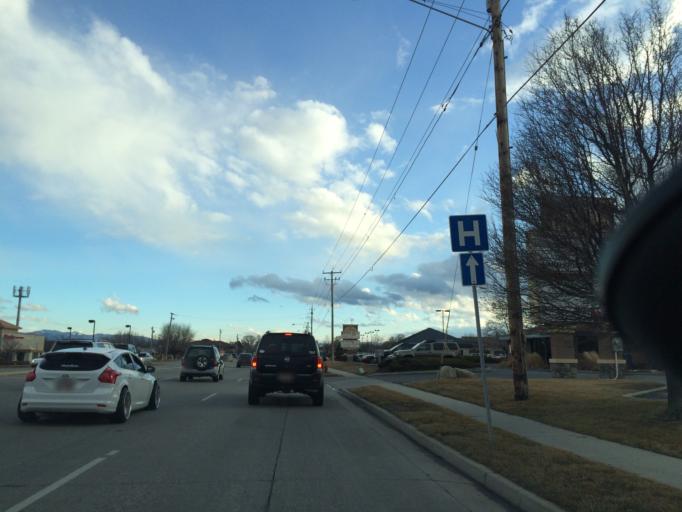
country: US
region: Utah
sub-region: Salt Lake County
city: West Jordan
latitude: 40.6231
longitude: -111.9389
